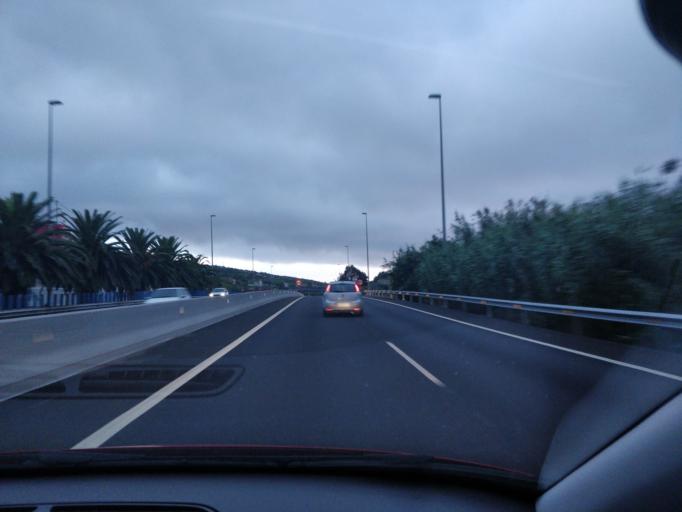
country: ES
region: Canary Islands
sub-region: Provincia de Santa Cruz de Tenerife
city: Tacoronte
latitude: 28.4795
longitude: -16.3995
